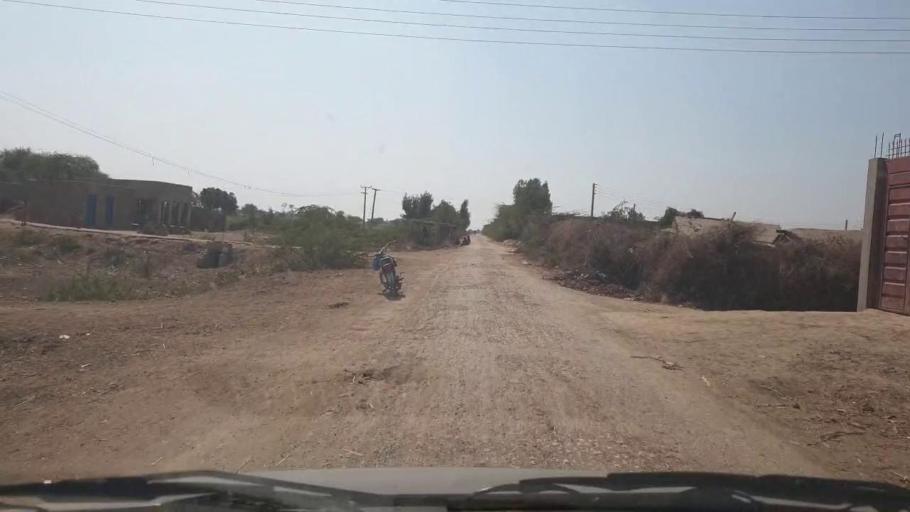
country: PK
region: Sindh
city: Samaro
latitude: 25.2312
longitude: 69.3367
